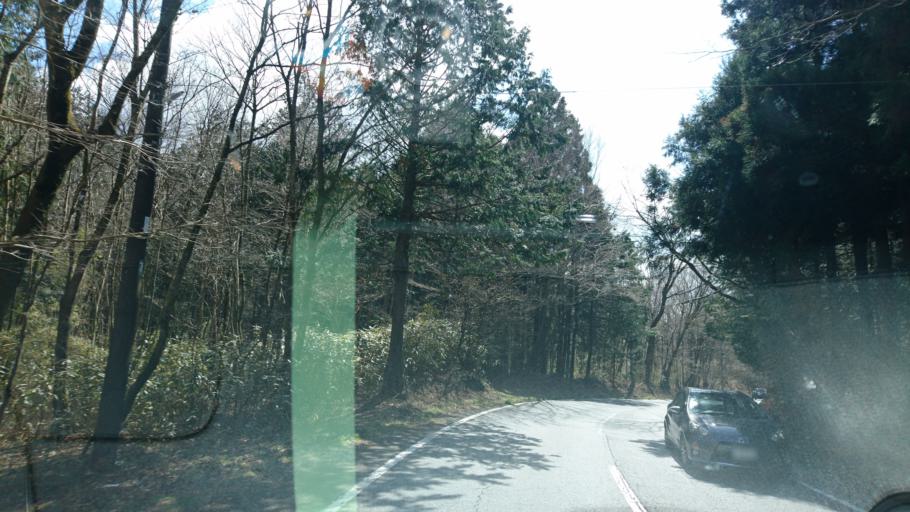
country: JP
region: Shizuoka
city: Fujinomiya
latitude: 35.3576
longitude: 138.6003
